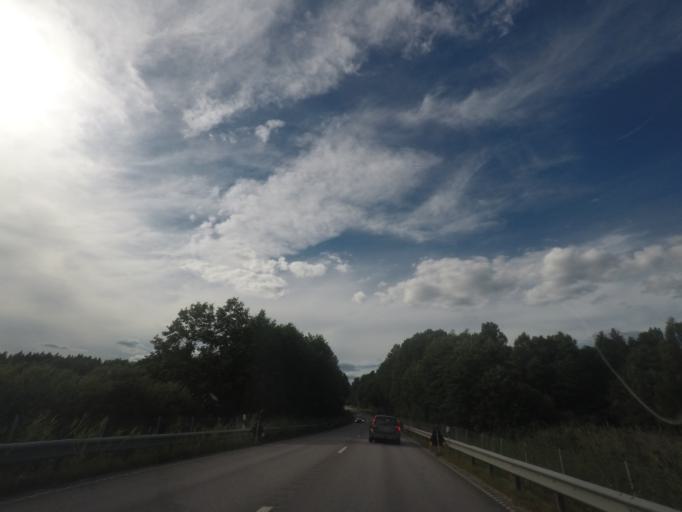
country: SE
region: Stockholm
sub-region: Norrtalje Kommun
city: Skanninge
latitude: 59.9037
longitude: 18.5883
